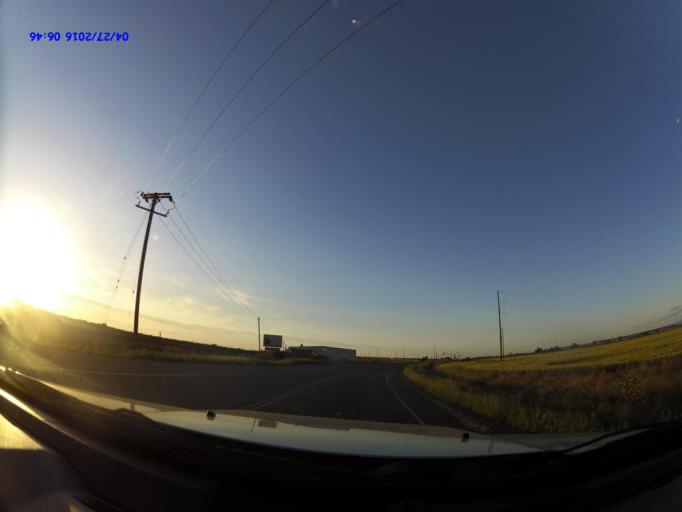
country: US
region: California
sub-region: San Joaquin County
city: Garden Acres
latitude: 37.9157
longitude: -121.1888
